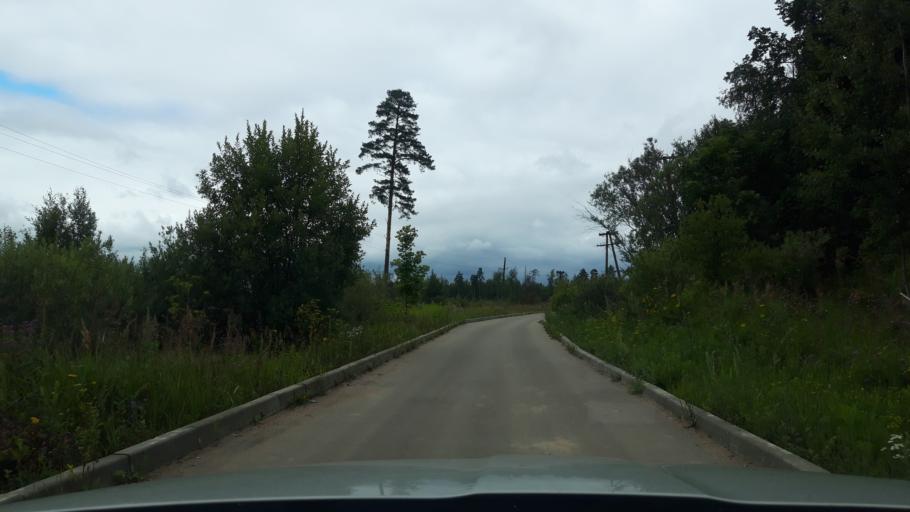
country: RU
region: Moskovskaya
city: Povarovo
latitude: 56.0453
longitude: 37.0549
